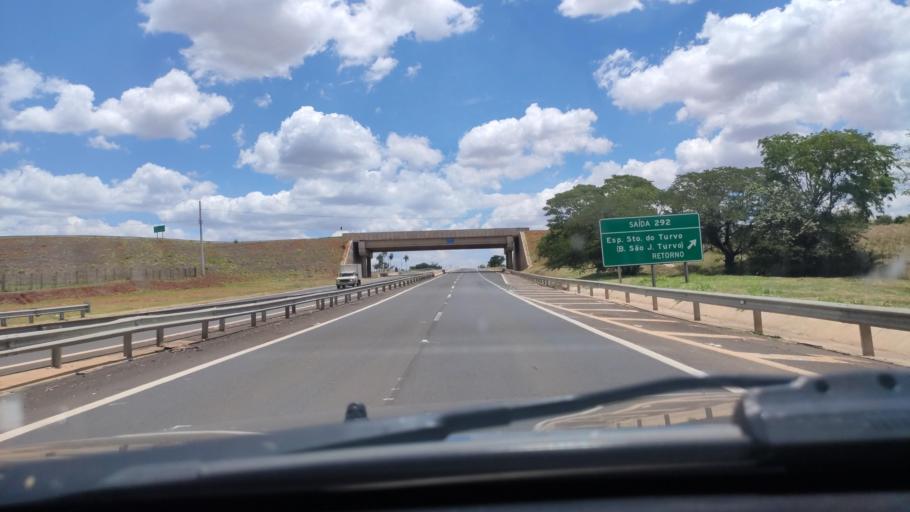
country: BR
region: Sao Paulo
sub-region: Duartina
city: Duartina
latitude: -22.6872
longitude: -49.4192
